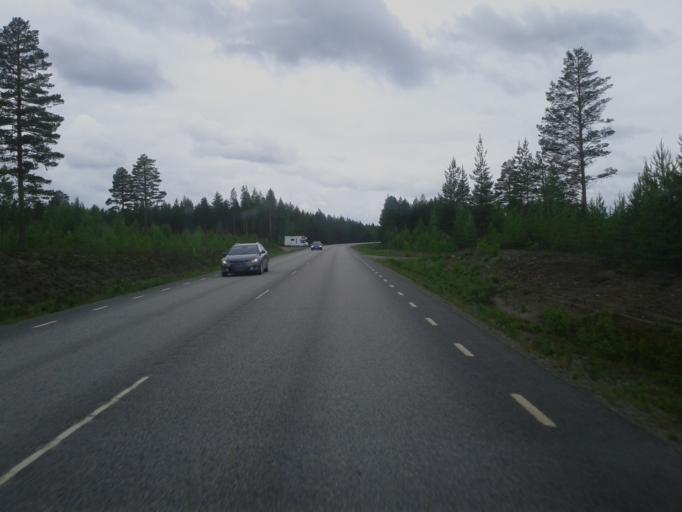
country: SE
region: Vaesterbotten
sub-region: Skelleftea Kommun
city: Langsele
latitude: 64.9335
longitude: 19.9636
